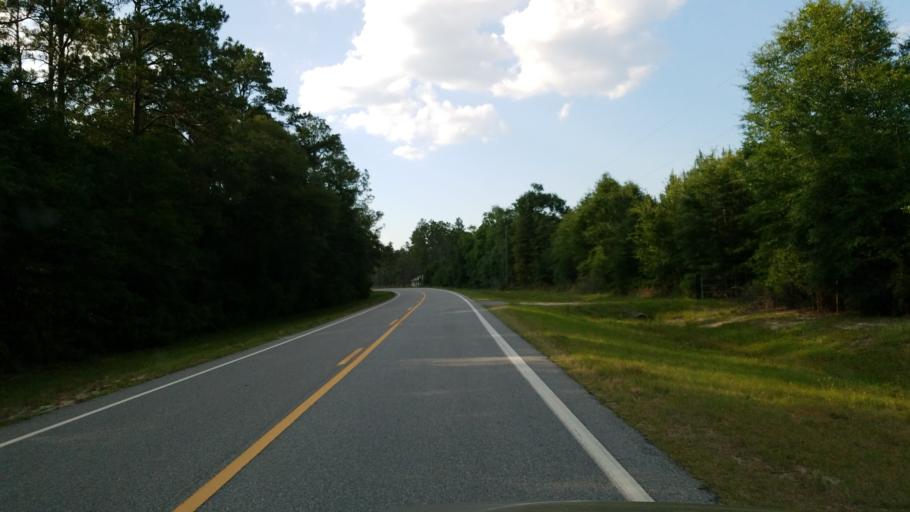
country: US
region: Georgia
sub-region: Echols County
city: Statenville
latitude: 30.7696
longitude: -83.0554
